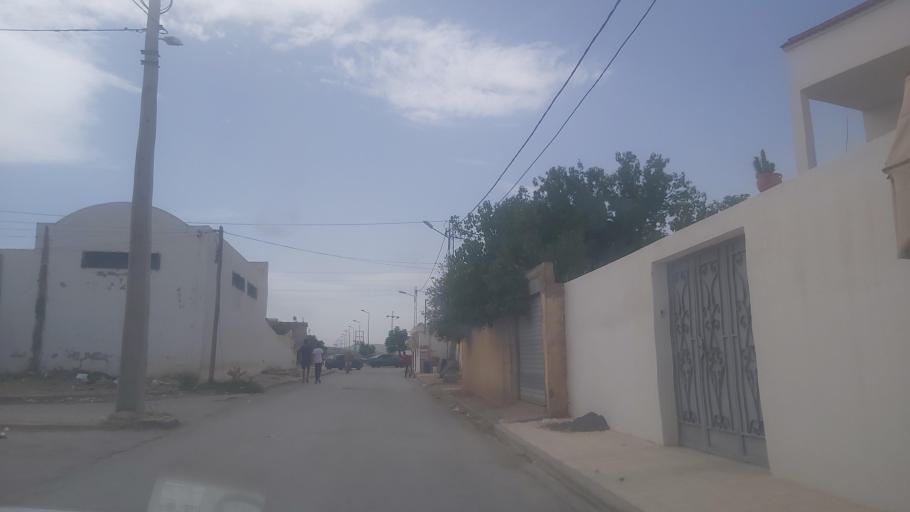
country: TN
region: Silyanah
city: Bu `Aradah
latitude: 36.3519
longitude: 9.6297
